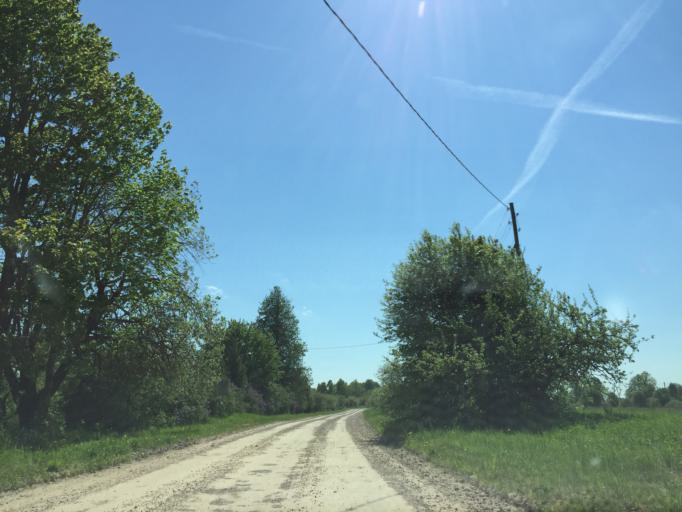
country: LV
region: Vecumnieki
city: Vecumnieki
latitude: 56.5882
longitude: 24.4834
